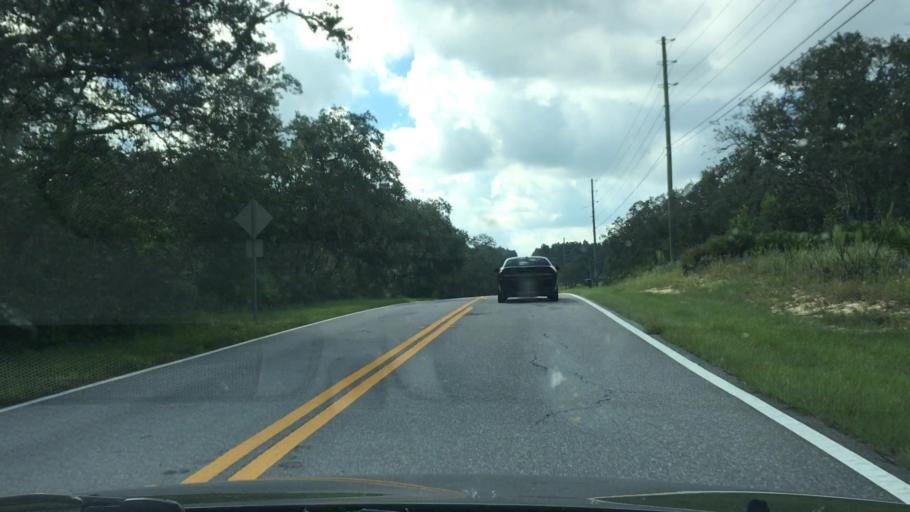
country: US
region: Florida
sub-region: Lake County
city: Astatula
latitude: 28.6647
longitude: -81.7303
